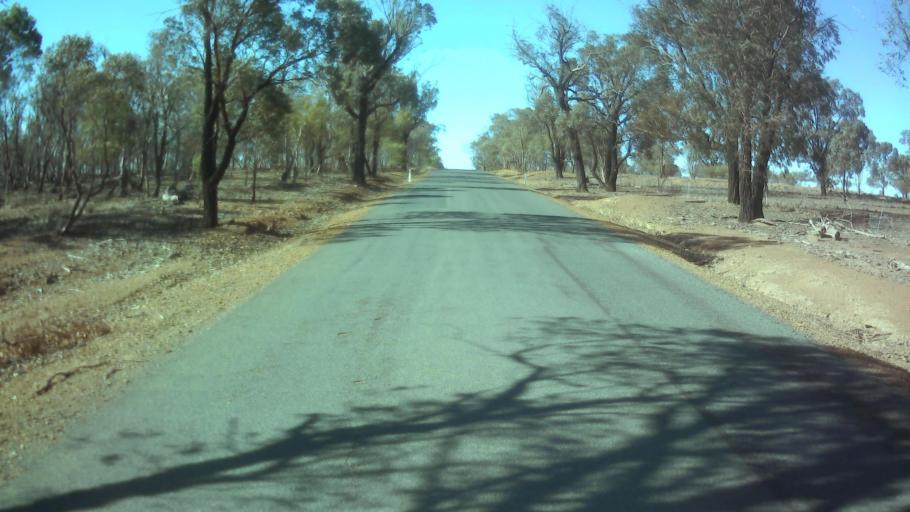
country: AU
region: New South Wales
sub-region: Forbes
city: Forbes
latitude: -33.7062
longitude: 147.8056
